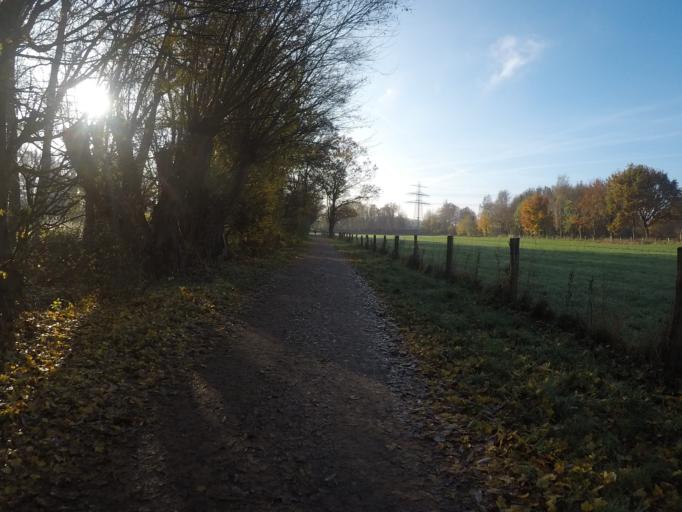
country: DE
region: Hamburg
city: Eidelstedt
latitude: 53.6118
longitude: 9.9215
